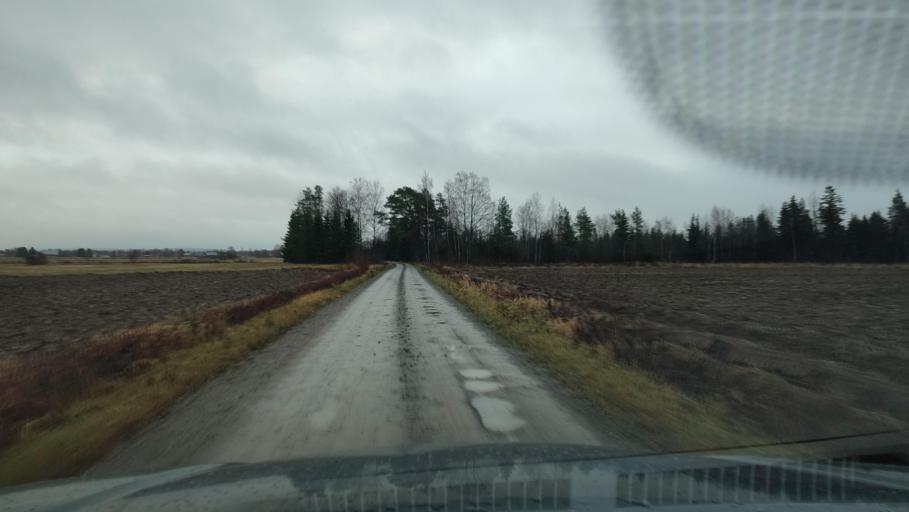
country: FI
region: Ostrobothnia
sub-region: Sydosterbotten
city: Kristinestad
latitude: 62.2429
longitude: 21.4842
